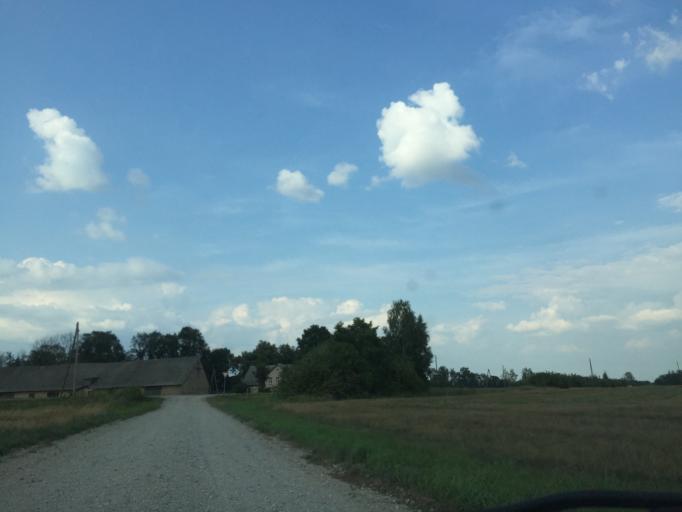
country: LT
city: Zagare
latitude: 56.4819
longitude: 23.1514
